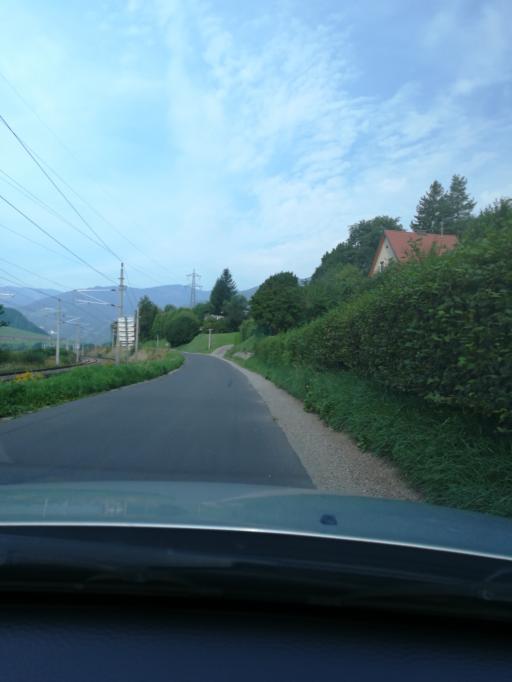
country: AT
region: Styria
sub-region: Politischer Bezirk Murtal
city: Sankt Georgen ob Judenburg
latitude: 47.2125
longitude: 14.4982
